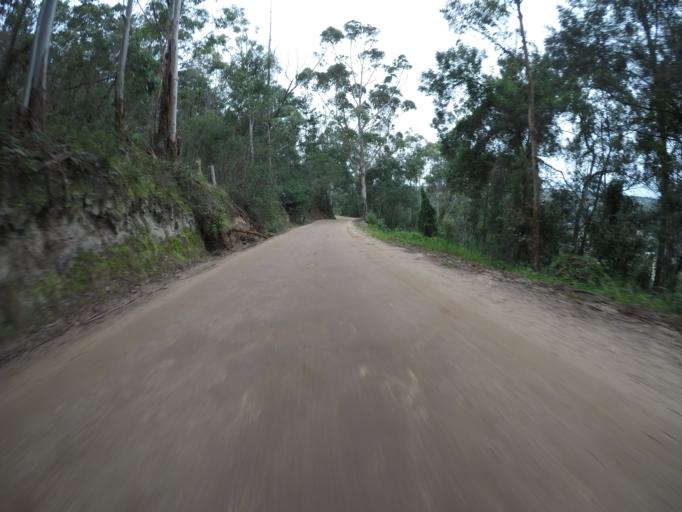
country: ZA
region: Western Cape
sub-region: Eden District Municipality
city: Knysna
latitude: -34.0122
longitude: 22.8080
